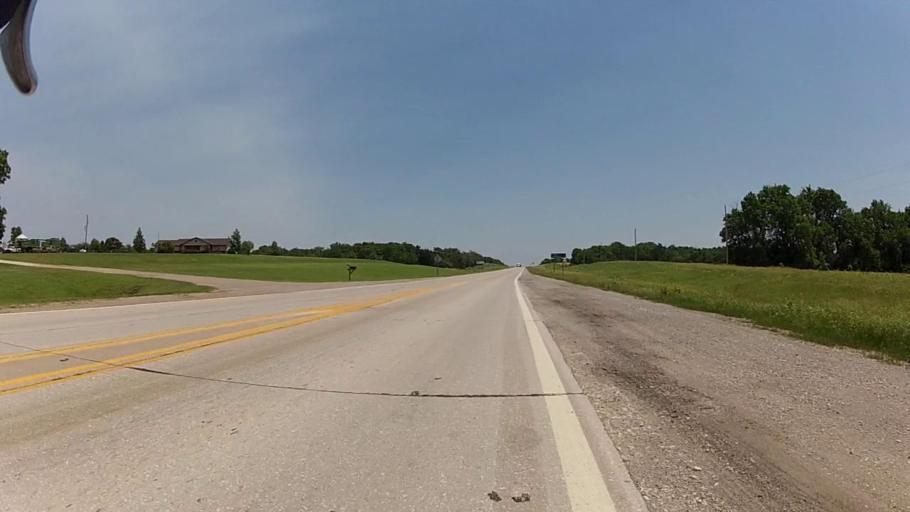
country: US
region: Kansas
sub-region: Sumner County
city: Caldwell
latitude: 37.0566
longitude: -97.3997
